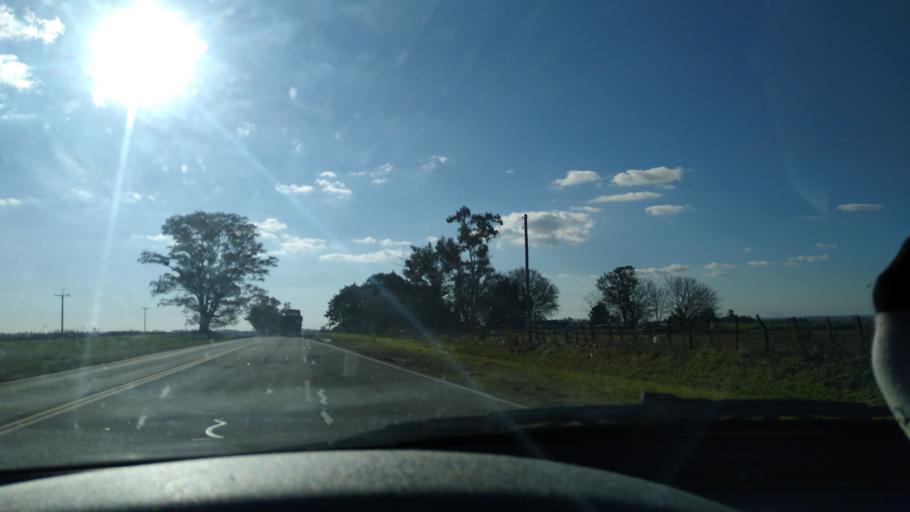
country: AR
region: Entre Rios
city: Diamante
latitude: -32.0980
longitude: -60.5885
